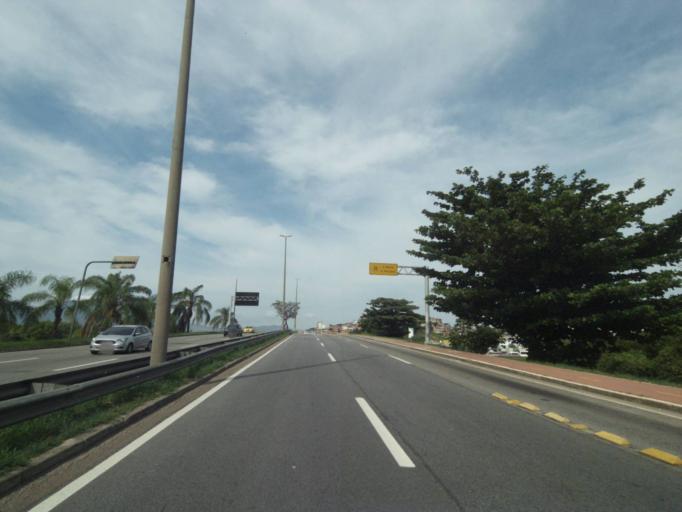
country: BR
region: Rio de Janeiro
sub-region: Rio De Janeiro
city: Rio de Janeiro
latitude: -22.8607
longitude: -43.2352
